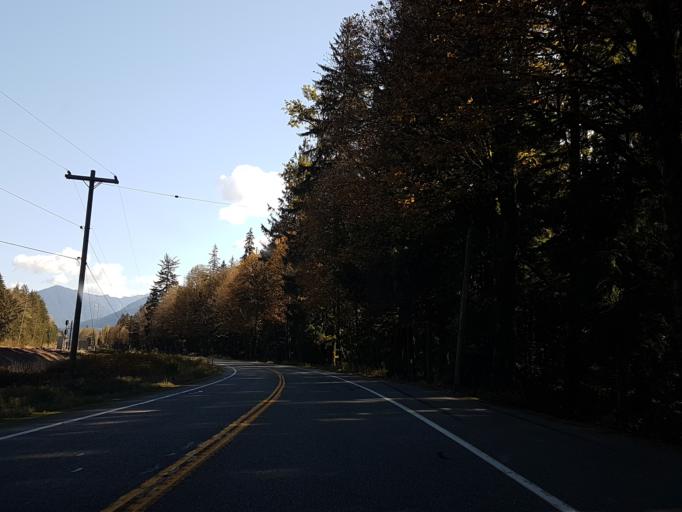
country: US
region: Washington
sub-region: Snohomish County
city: Gold Bar
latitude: 47.7816
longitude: -121.4966
